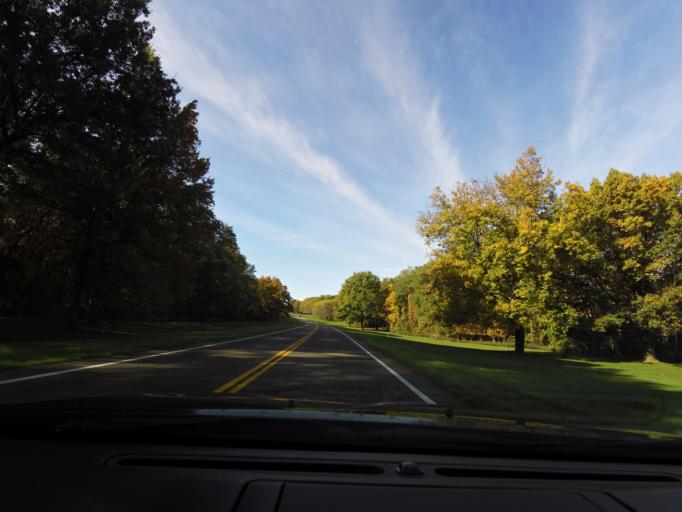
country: US
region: New York
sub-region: Livingston County
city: Mount Morris
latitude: 42.7380
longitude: -77.9007
